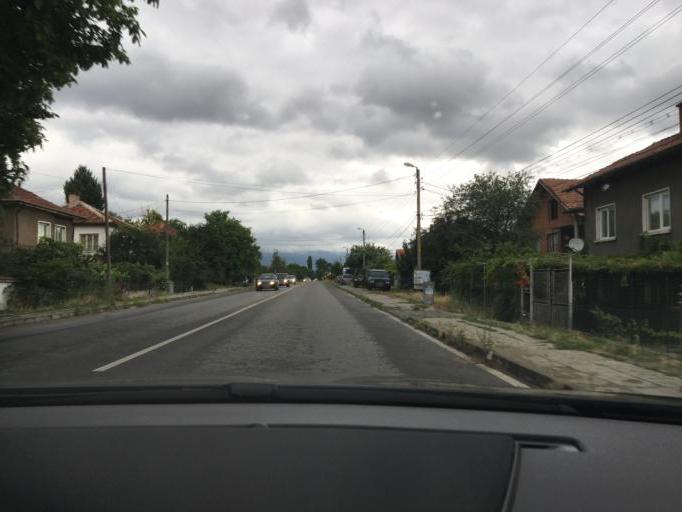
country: BG
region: Kyustendil
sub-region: Obshtina Kyustendil
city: Kyustendil
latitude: 42.2787
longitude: 22.7368
